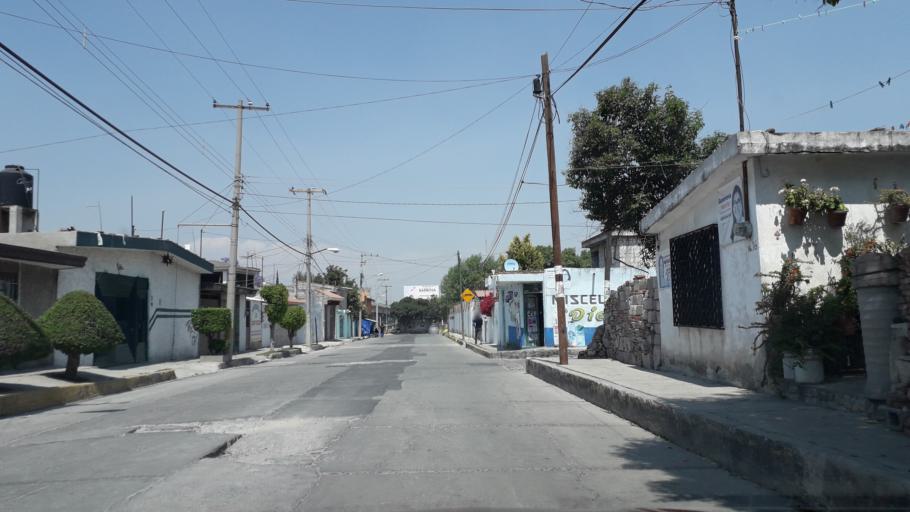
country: MX
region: Puebla
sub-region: Cuautlancingo
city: Sanctorum
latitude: 19.0918
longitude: -98.2204
